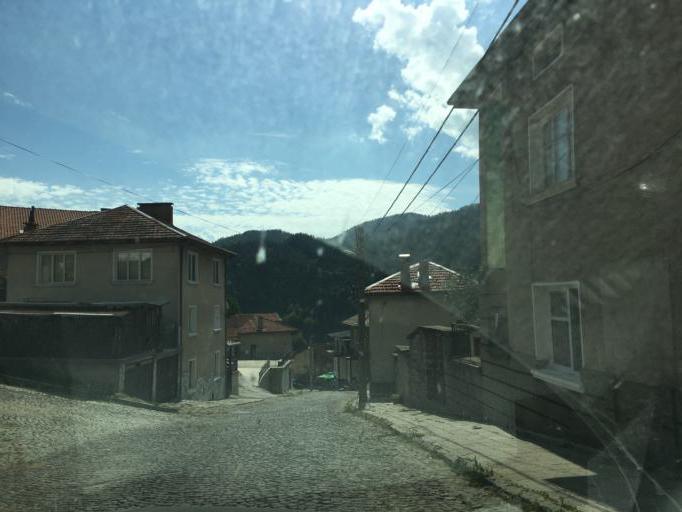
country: BG
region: Pazardzhik
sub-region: Obshtina Bratsigovo
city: Bratsigovo
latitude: 41.8841
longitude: 24.3496
